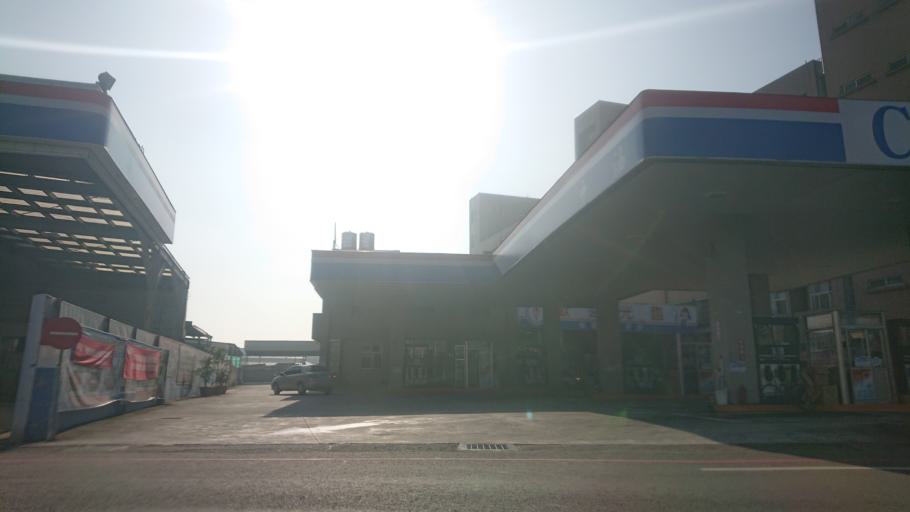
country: TW
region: Taiwan
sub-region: Tainan
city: Tainan
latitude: 23.0171
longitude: 120.2385
